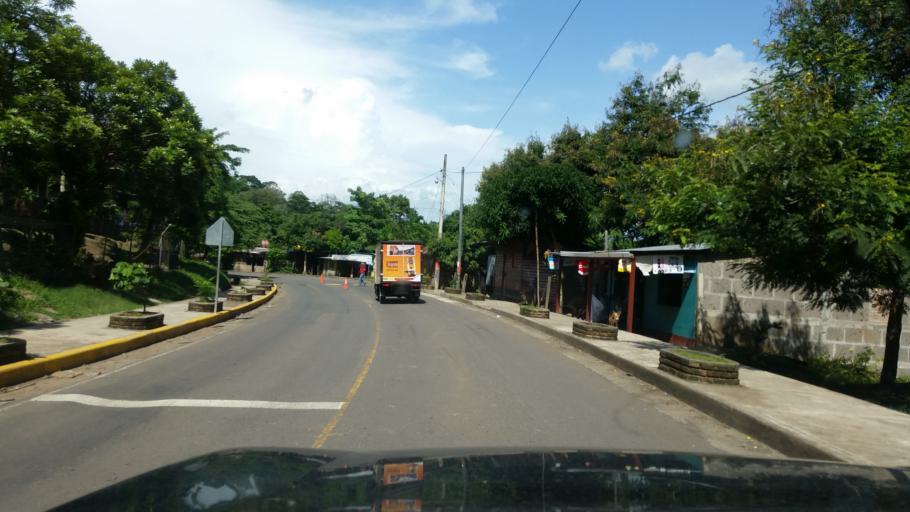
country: NI
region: Matagalpa
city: San Ramon
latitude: 13.0058
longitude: -85.8082
